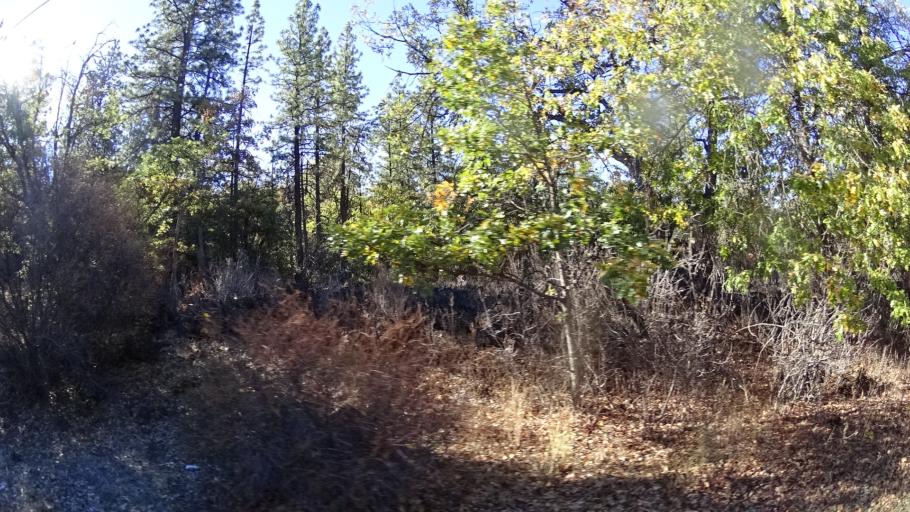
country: US
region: California
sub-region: Siskiyou County
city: Montague
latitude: 41.9846
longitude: -122.3582
